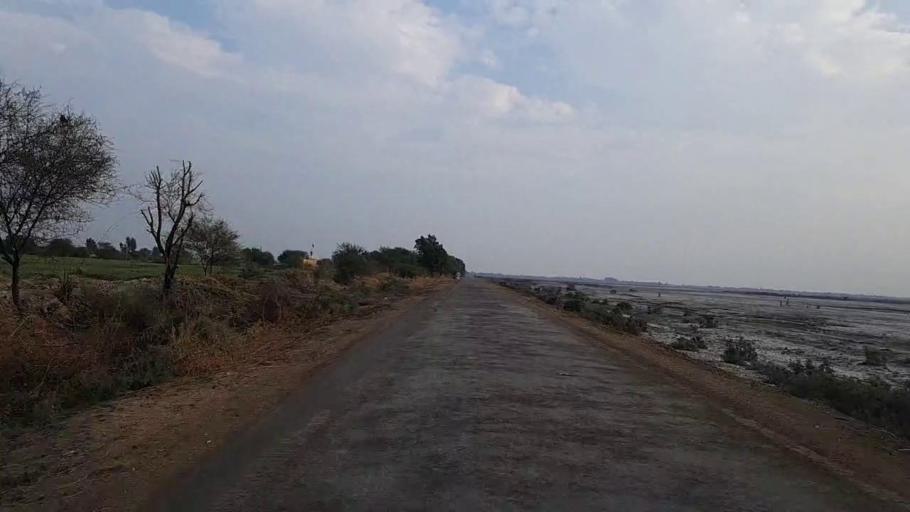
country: PK
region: Sindh
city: Pithoro
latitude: 25.4792
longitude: 69.2659
